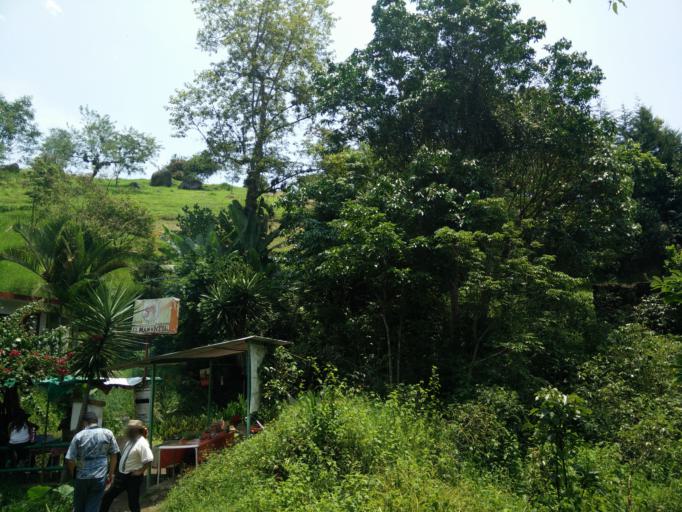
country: MX
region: Veracruz
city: Xico
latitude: 19.4017
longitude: -96.9975
